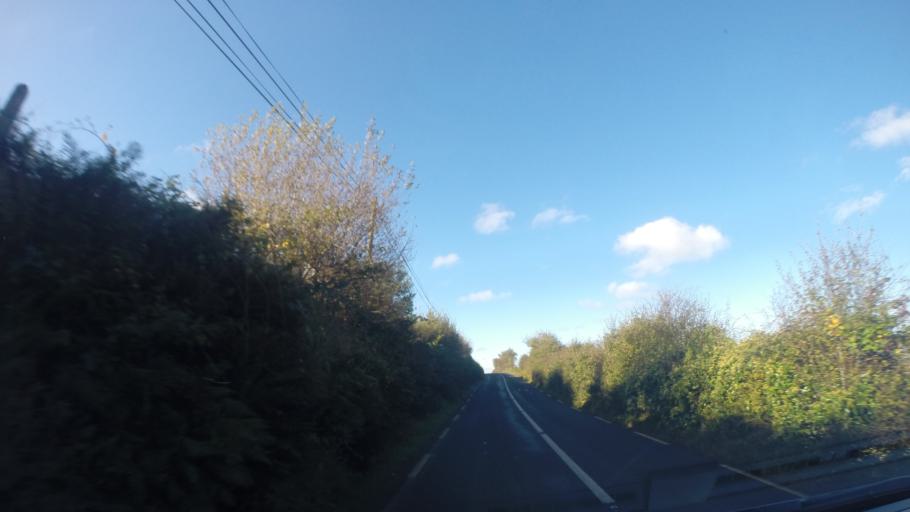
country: IE
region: Ulster
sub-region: County Donegal
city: Dungloe
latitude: 54.8343
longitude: -8.3599
